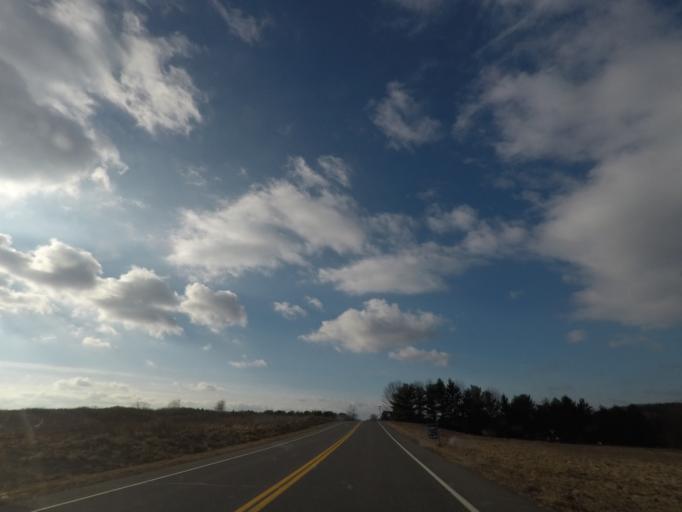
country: US
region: New York
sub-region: Albany County
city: Voorheesville
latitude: 42.6585
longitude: -73.8995
